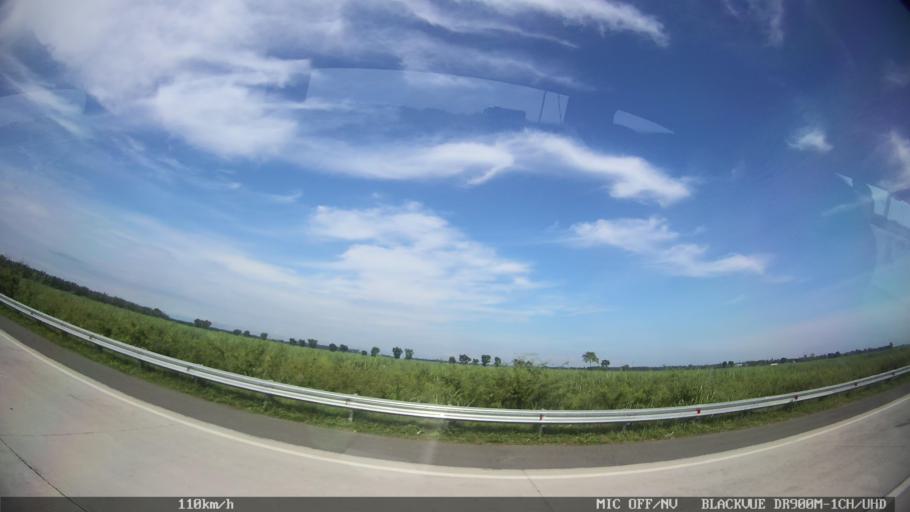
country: ID
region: North Sumatra
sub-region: Kabupaten Langkat
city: Stabat
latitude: 3.6924
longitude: 98.5406
